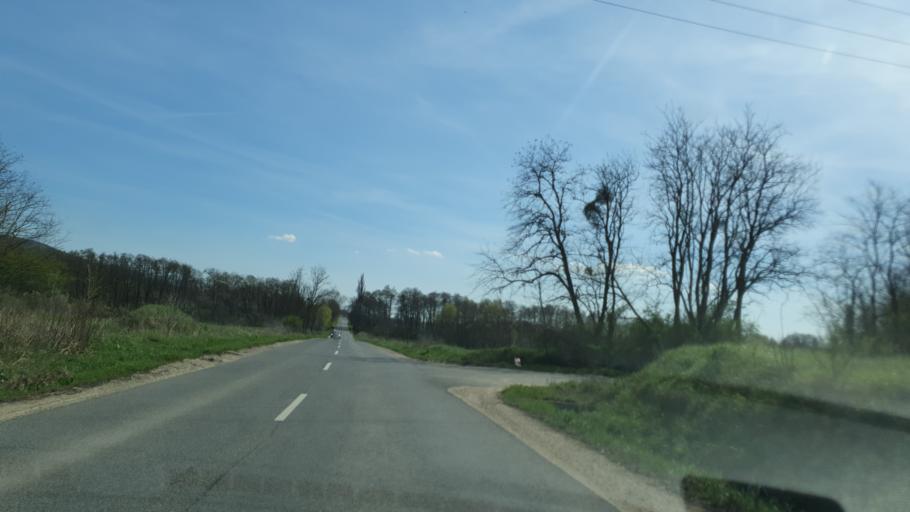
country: HU
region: Fejer
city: Pusztavam
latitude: 47.4165
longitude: 18.2206
